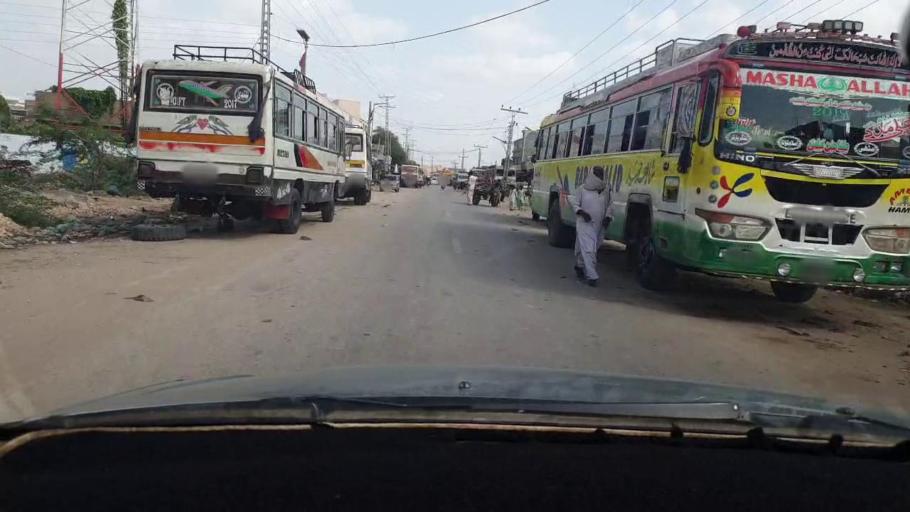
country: PK
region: Sindh
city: Naukot
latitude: 24.8573
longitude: 69.3980
